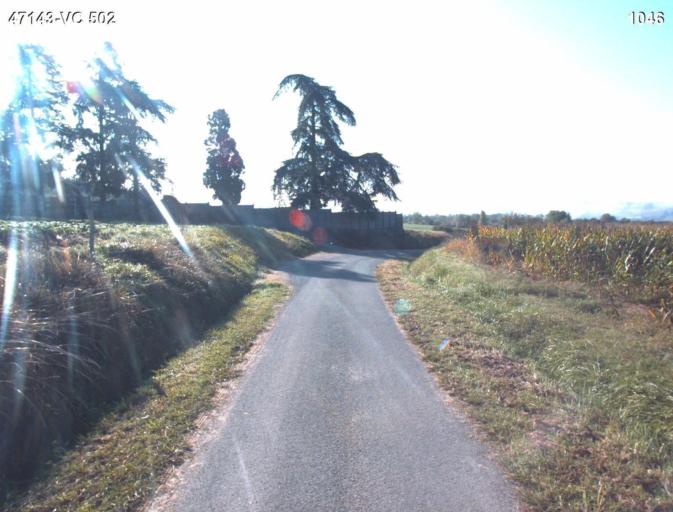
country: FR
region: Aquitaine
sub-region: Departement du Lot-et-Garonne
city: Vianne
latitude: 44.1729
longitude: 0.3269
